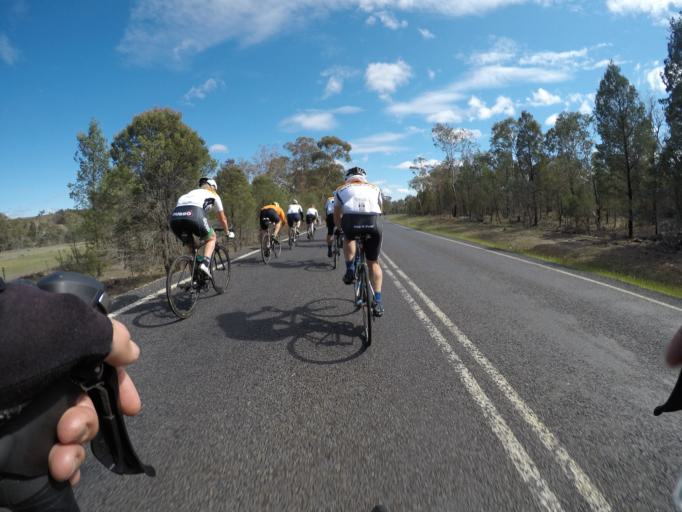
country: AU
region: New South Wales
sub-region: Parkes
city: Peak Hill
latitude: -32.7148
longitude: 148.5521
